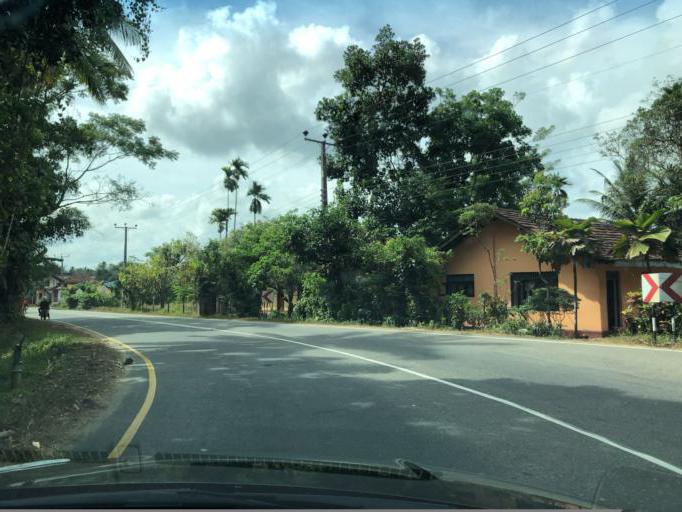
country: LK
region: Western
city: Horana South
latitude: 6.6413
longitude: 80.0799
